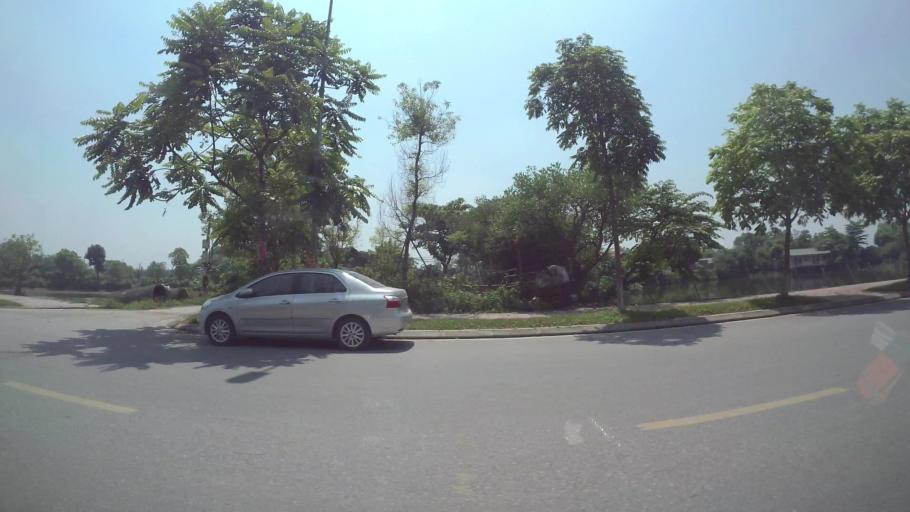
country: VN
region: Ha Noi
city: Hoan Kiem
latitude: 21.0370
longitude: 105.8816
